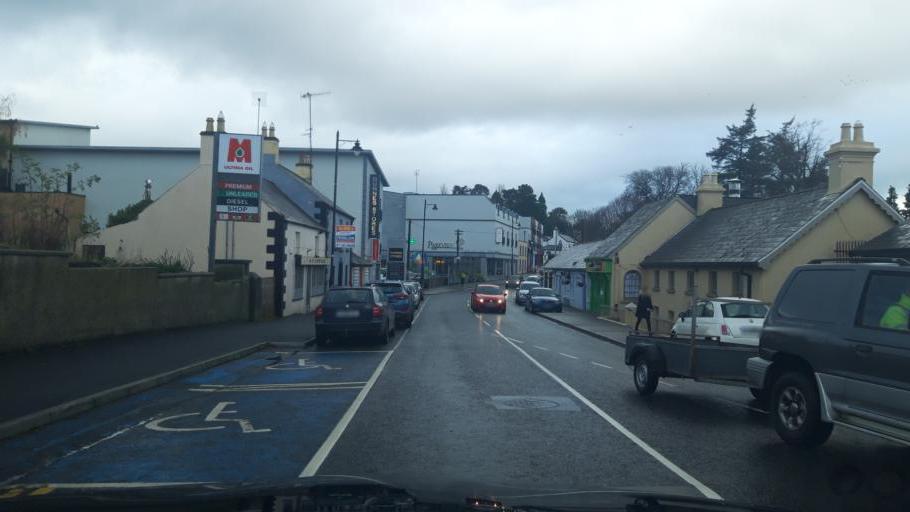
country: IE
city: Newtownmountkennedy
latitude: 53.0912
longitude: -6.1119
